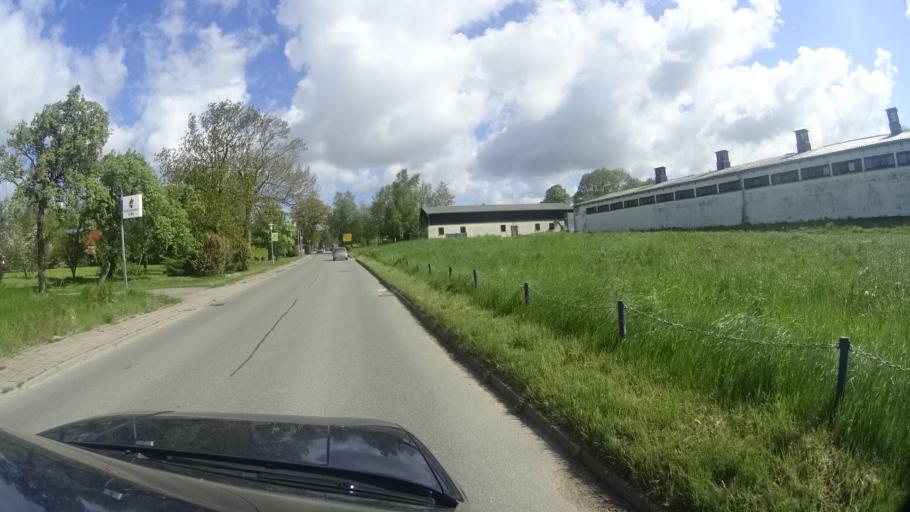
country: DE
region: Mecklenburg-Vorpommern
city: Trinwillershagen
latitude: 54.3000
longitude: 12.5822
